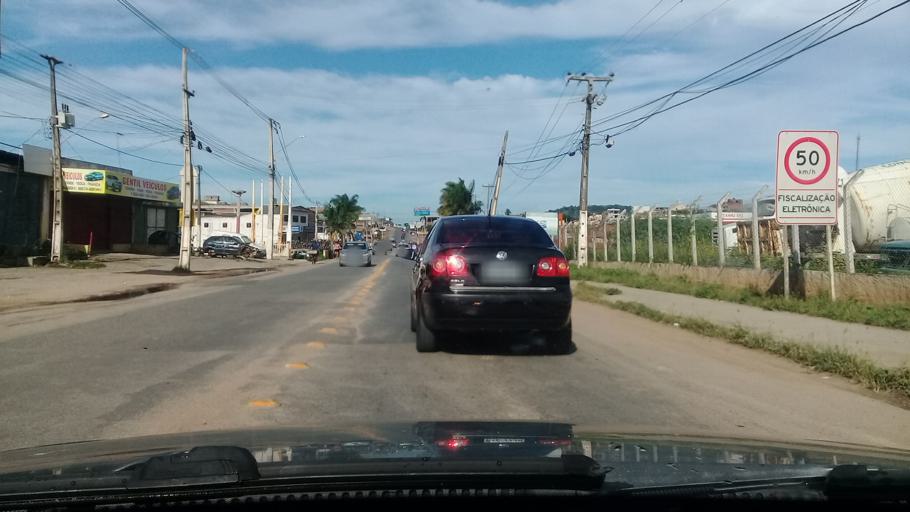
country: BR
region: Pernambuco
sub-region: Vitoria De Santo Antao
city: Vitoria de Santo Antao
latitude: -8.1141
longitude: -35.2839
